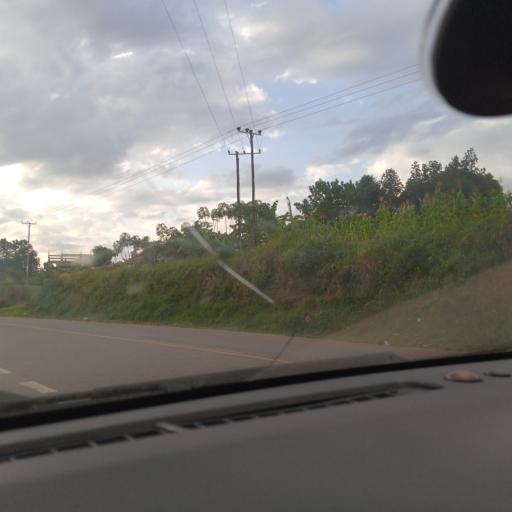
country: UG
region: Central Region
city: Masaka
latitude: -0.3369
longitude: 31.6900
